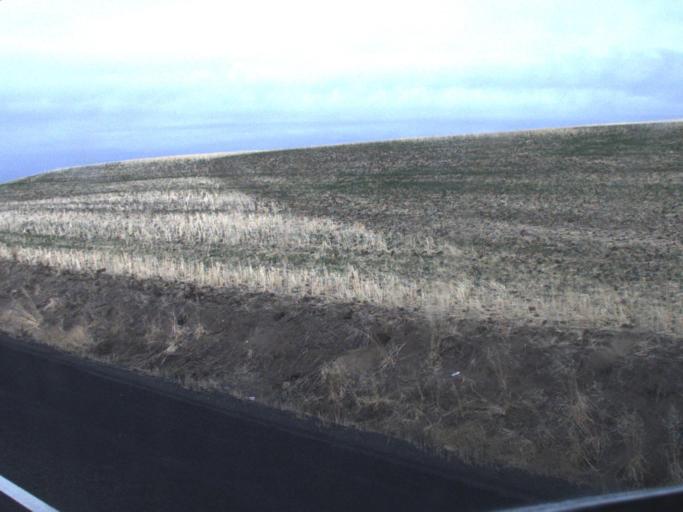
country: US
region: Washington
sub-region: Whitman County
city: Pullman
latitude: 46.5905
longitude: -117.1712
